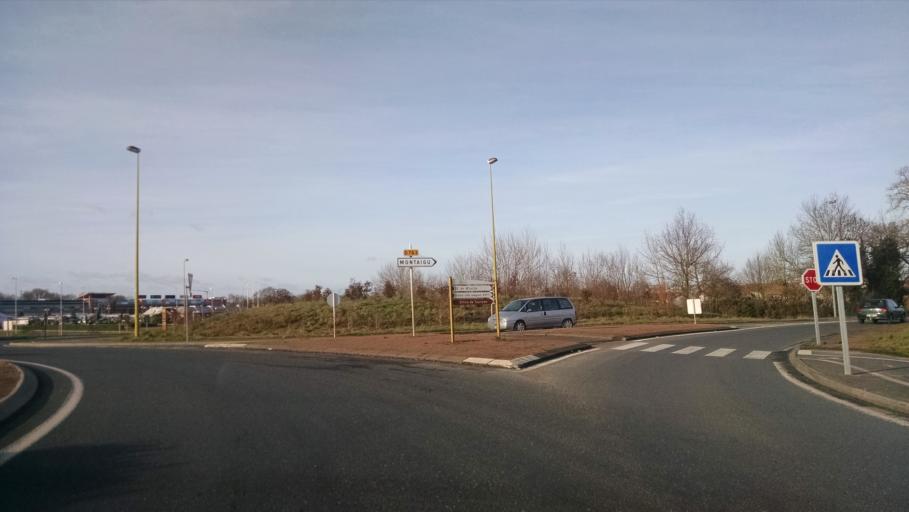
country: FR
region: Pays de la Loire
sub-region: Departement de la Vendee
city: Bouffere
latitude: 46.9692
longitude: -1.3293
